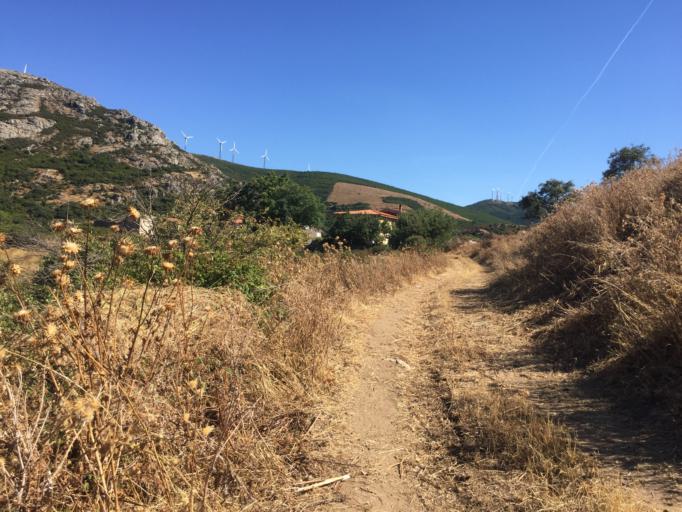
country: IT
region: Sardinia
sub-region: Provincia di Olbia-Tempio
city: Aggius
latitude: 40.9517
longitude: 8.9908
